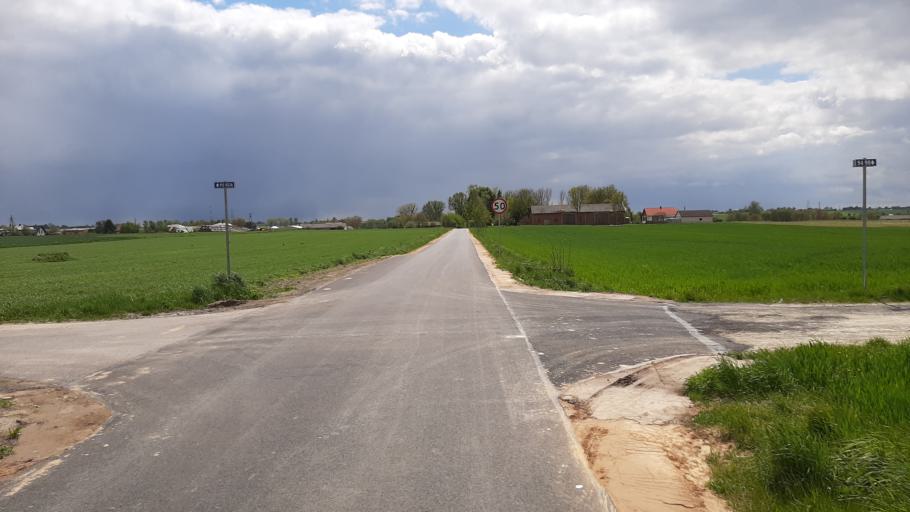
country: PL
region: Lublin Voivodeship
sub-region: Powiat lubelski
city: Garbow
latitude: 51.3577
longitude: 22.3957
